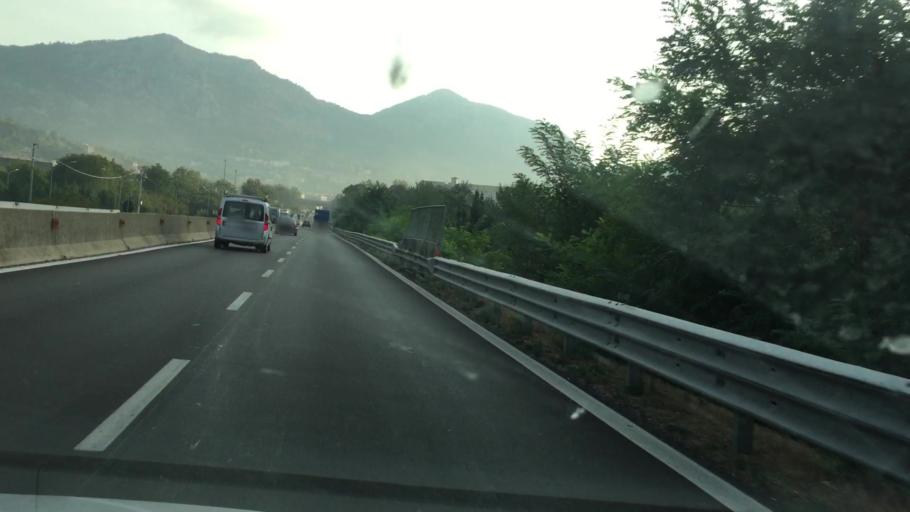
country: IT
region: Campania
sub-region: Provincia di Avellino
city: Torchiati
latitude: 40.8264
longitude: 14.8127
